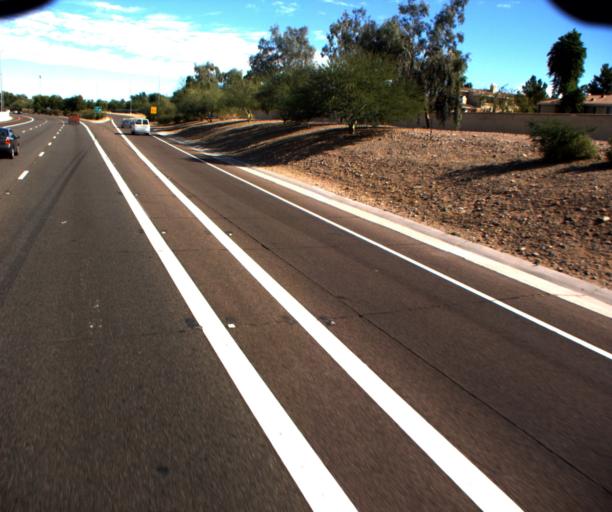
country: US
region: Arizona
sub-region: Maricopa County
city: Sun City
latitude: 33.6478
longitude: -112.2333
